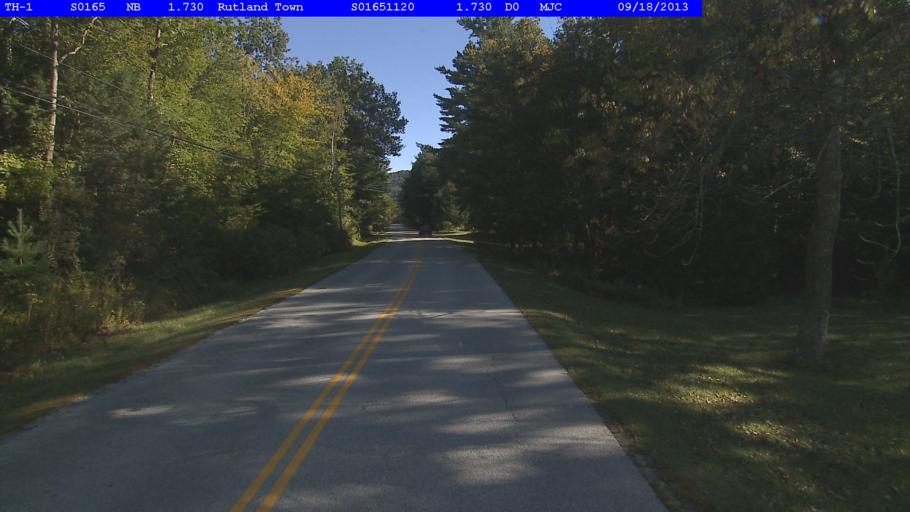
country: US
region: Vermont
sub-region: Rutland County
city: Rutland
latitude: 43.6643
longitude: -72.9483
